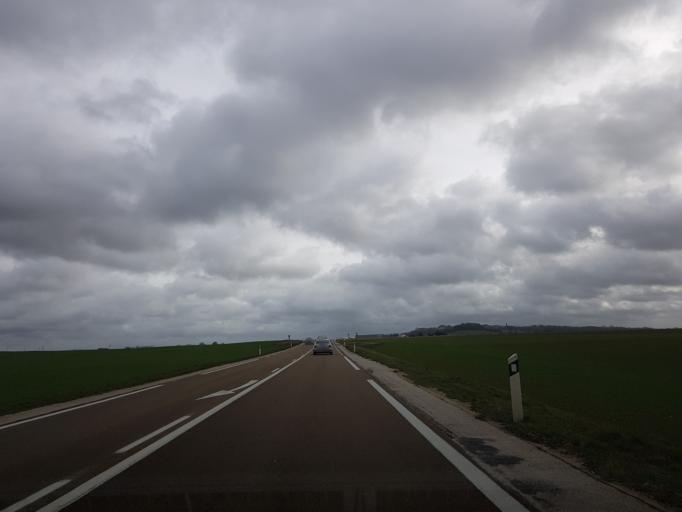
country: FR
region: Champagne-Ardenne
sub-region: Departement de la Haute-Marne
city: Langres
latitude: 47.8975
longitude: 5.3098
